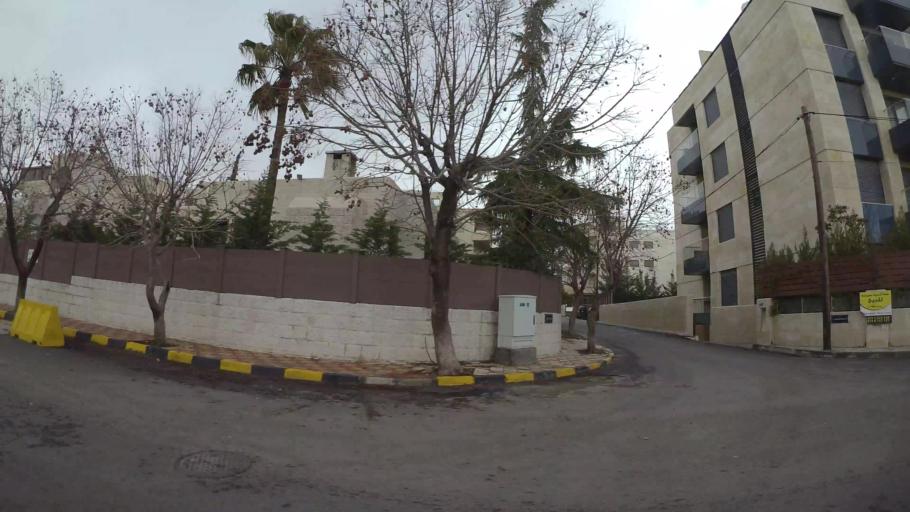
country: JO
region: Amman
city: Wadi as Sir
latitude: 31.9511
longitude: 35.8730
